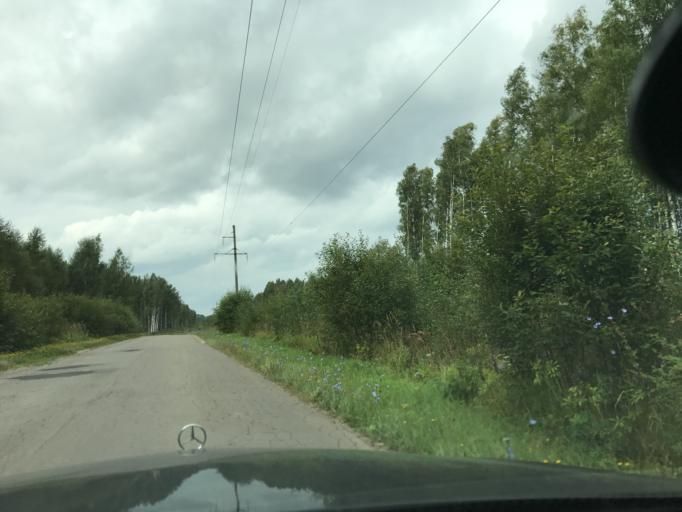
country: RU
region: Vladimir
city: Galitsy
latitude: 55.9967
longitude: 42.8273
